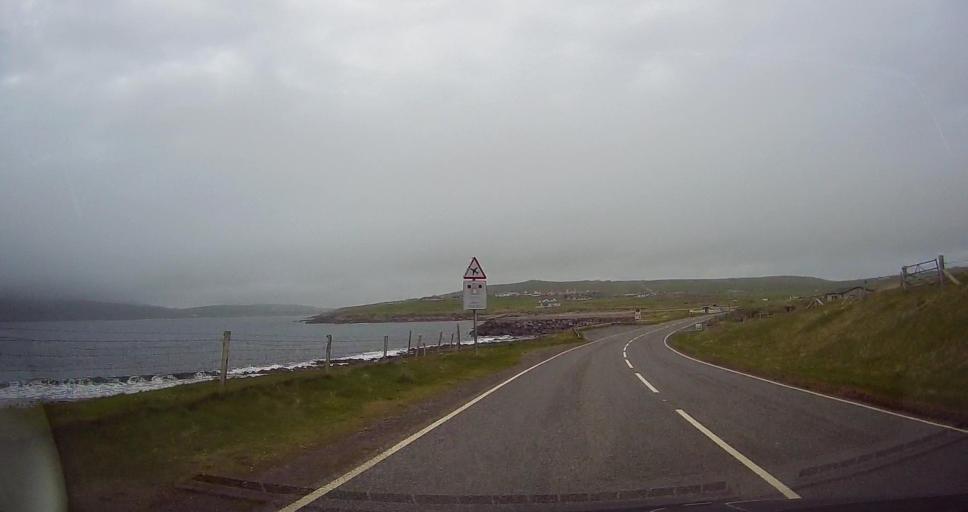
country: GB
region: Scotland
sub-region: Shetland Islands
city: Sandwick
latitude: 59.8777
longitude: -1.3070
